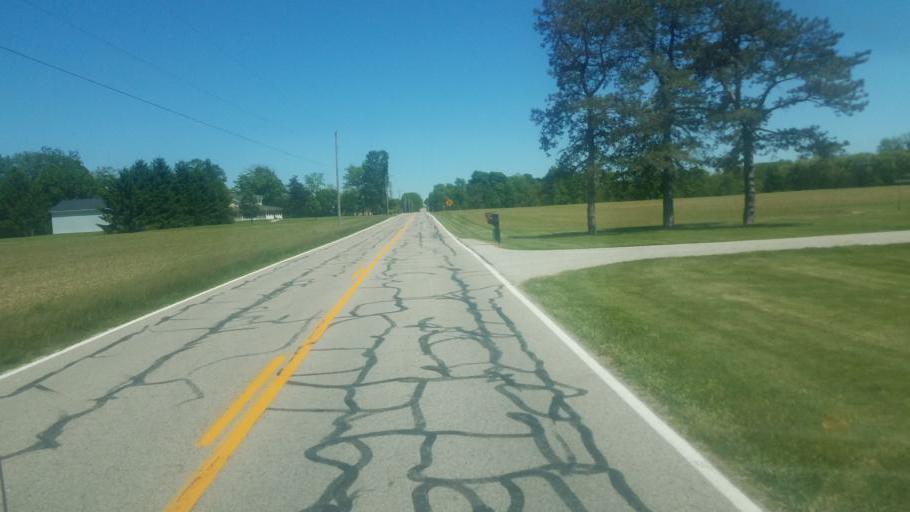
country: US
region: Ohio
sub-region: Shelby County
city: Sidney
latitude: 40.2148
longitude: -84.1751
